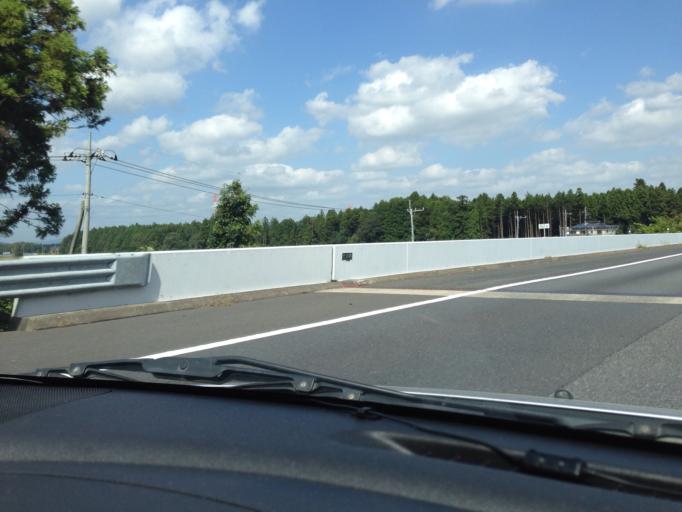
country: JP
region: Ibaraki
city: Tomobe
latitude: 36.2716
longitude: 140.3056
